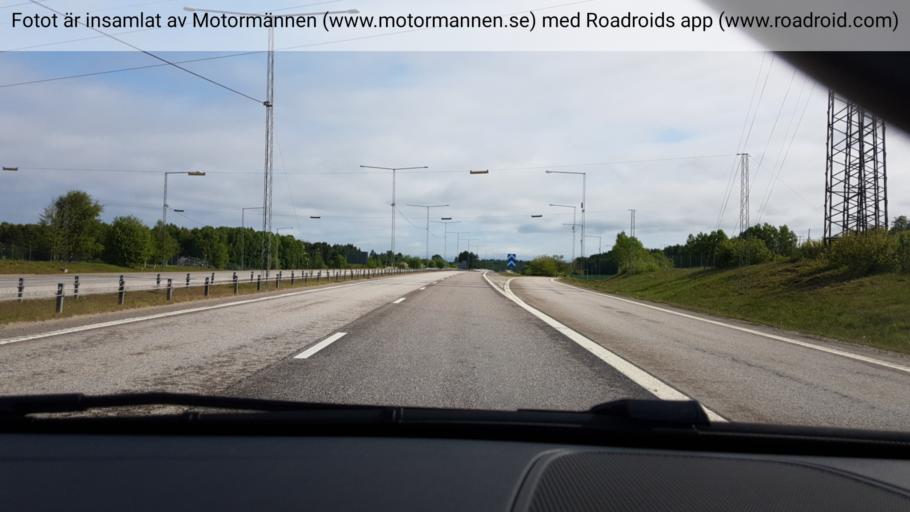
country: SE
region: Stockholm
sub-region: Haninge Kommun
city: Jordbro
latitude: 59.1191
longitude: 18.1299
